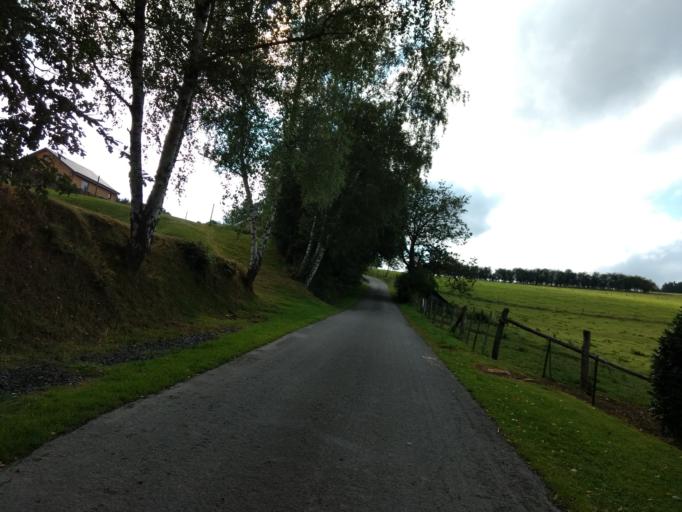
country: BE
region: Wallonia
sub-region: Province du Luxembourg
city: Houffalize
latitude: 50.1496
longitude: 5.7404
